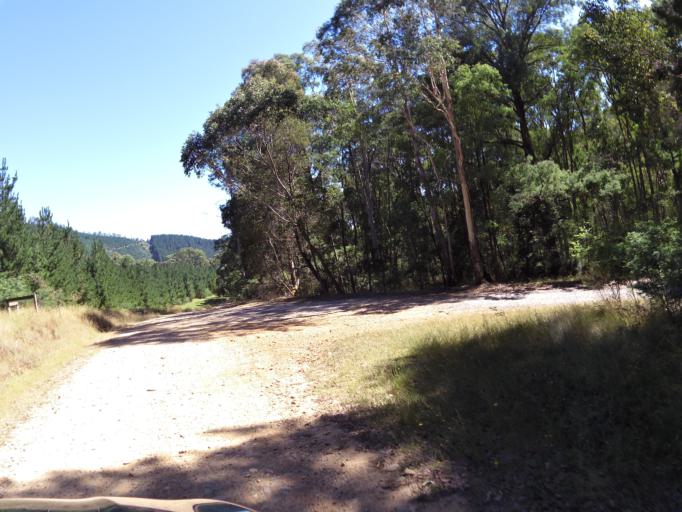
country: AU
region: Victoria
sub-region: Alpine
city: Mount Beauty
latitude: -36.7498
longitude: 146.9546
